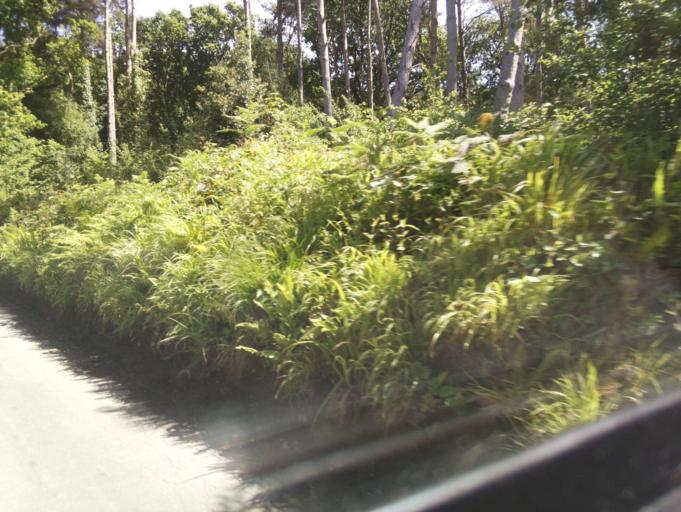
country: GB
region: England
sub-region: Devon
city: Budleigh Salterton
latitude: 50.6299
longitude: -3.3537
